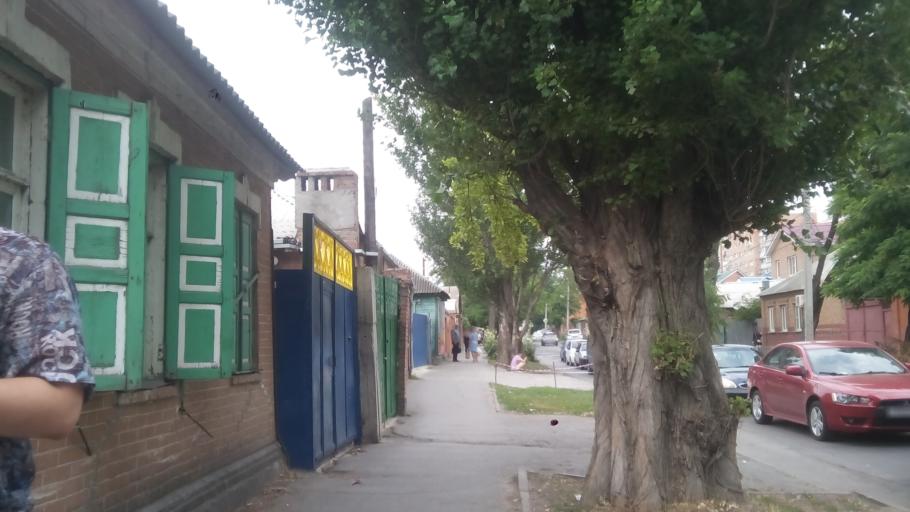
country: RU
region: Rostov
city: Rostov-na-Donu
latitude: 47.2120
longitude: 39.6736
